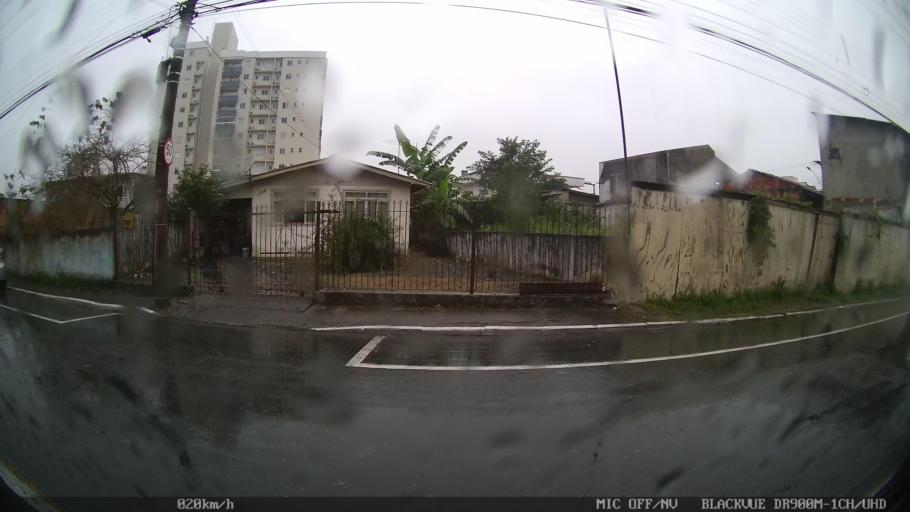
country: BR
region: Santa Catarina
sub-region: Itajai
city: Itajai
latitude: -26.9164
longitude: -48.6833
